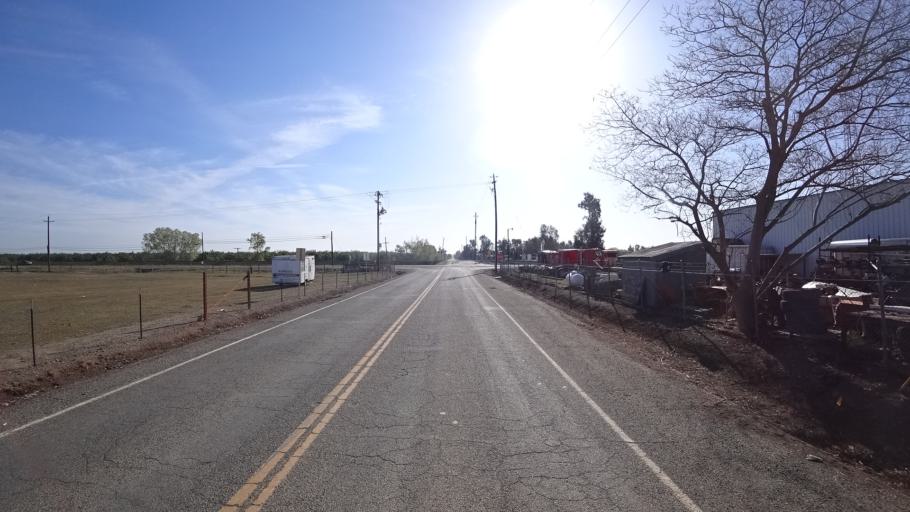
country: US
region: California
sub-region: Glenn County
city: Willows
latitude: 39.5388
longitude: -122.1943
